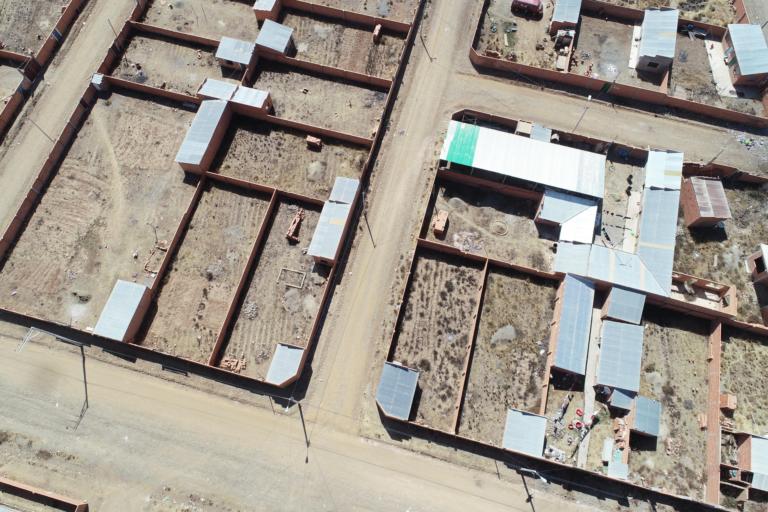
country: BO
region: La Paz
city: La Paz
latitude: -16.5944
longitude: -68.2098
